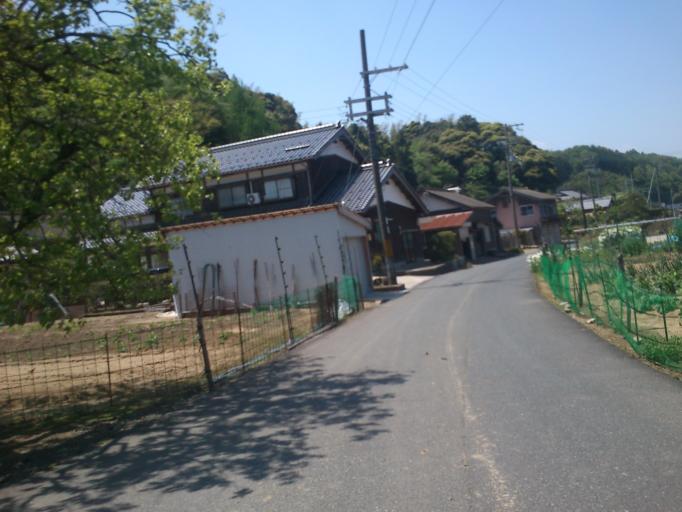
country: JP
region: Kyoto
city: Miyazu
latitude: 35.7152
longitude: 135.1181
